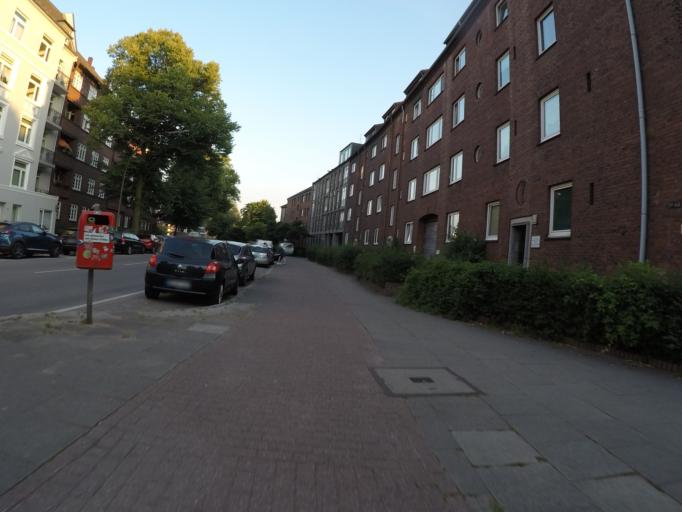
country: DE
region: Hamburg
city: Barmbek-Nord
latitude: 53.5868
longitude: 10.0413
